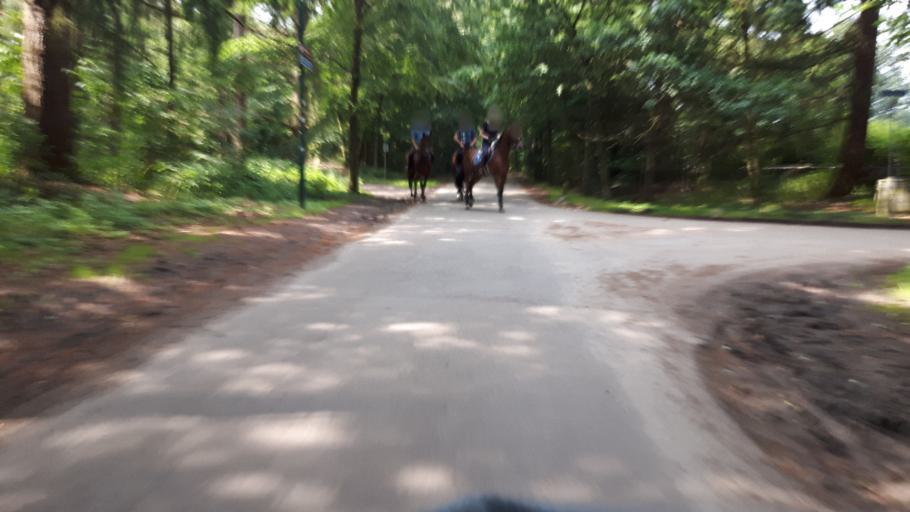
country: NL
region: Utrecht
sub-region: Gemeente Soest
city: Soest
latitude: 52.1571
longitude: 5.2828
